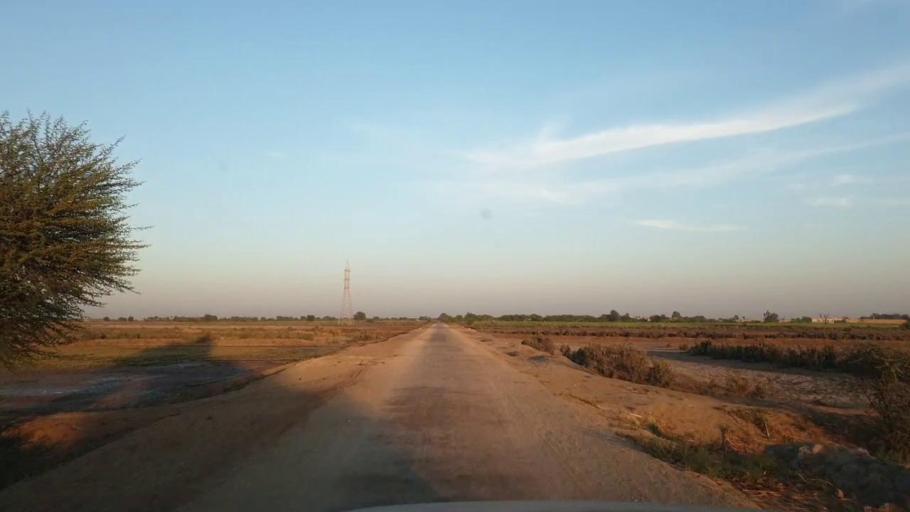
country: PK
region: Sindh
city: Kunri
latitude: 25.1375
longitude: 69.4368
